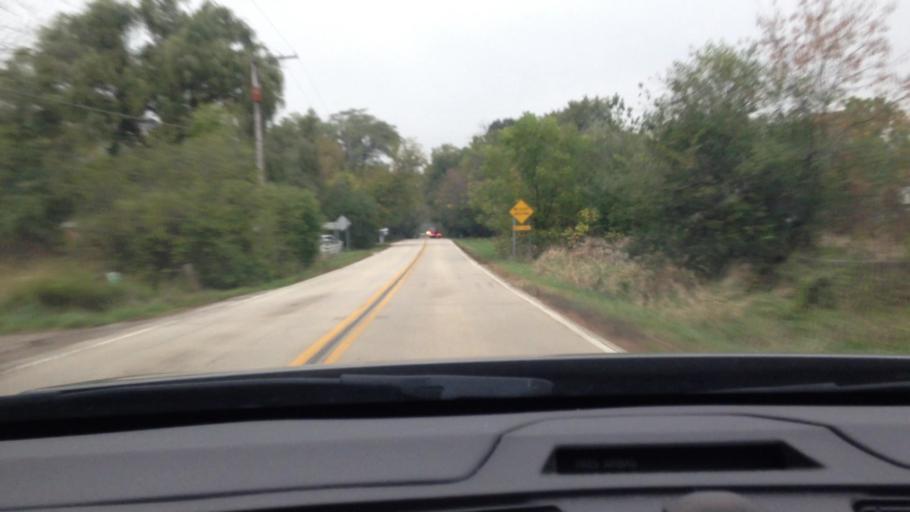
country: US
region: Illinois
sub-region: Cook County
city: Barrington Hills
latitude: 42.0962
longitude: -88.1946
